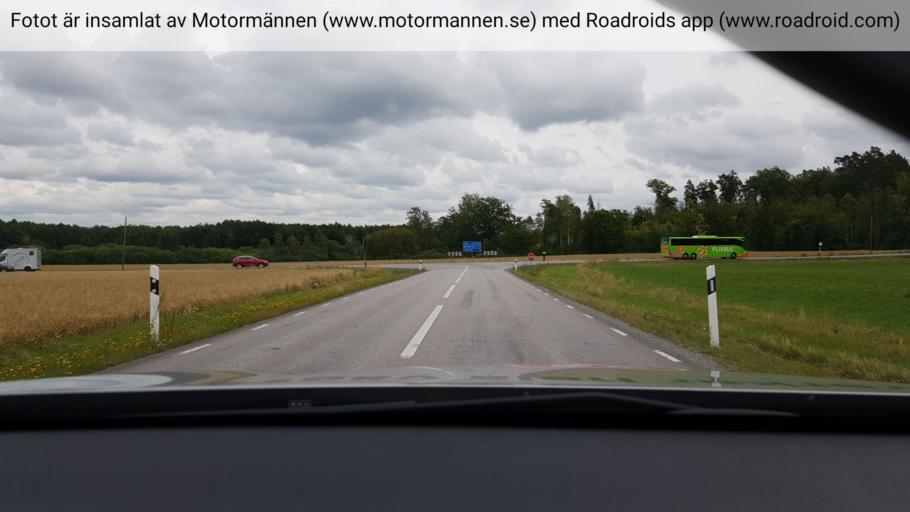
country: SE
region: Stockholm
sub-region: Sigtuna Kommun
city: Sigtuna
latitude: 59.6582
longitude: 17.6866
